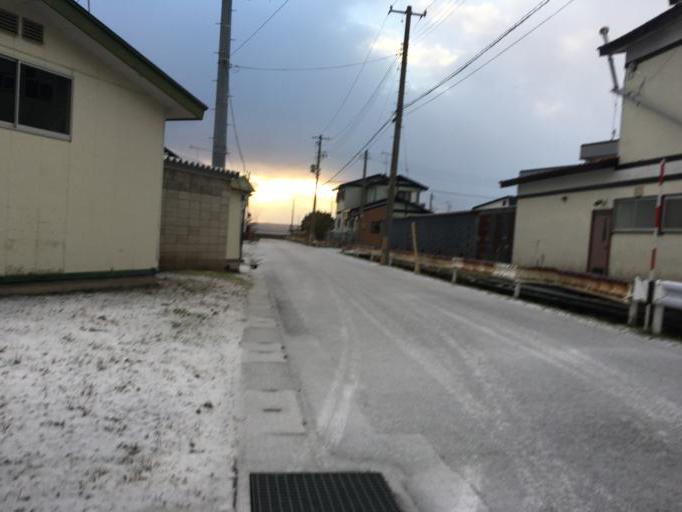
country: JP
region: Aomori
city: Mutsu
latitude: 41.2776
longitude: 141.1576
